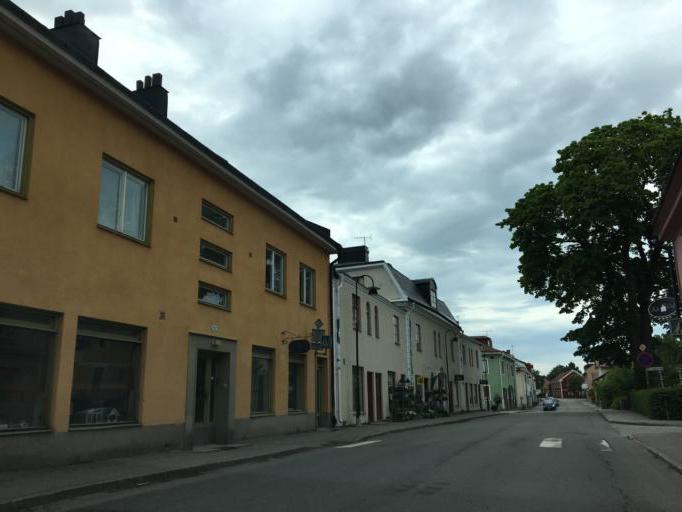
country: SE
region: Soedermanland
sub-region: Flens Kommun
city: Malmkoping
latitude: 59.1327
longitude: 16.7284
